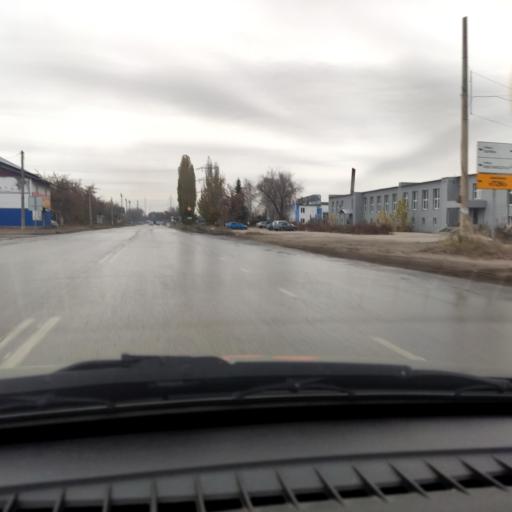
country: RU
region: Samara
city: Tol'yatti
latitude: 53.5239
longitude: 49.4706
